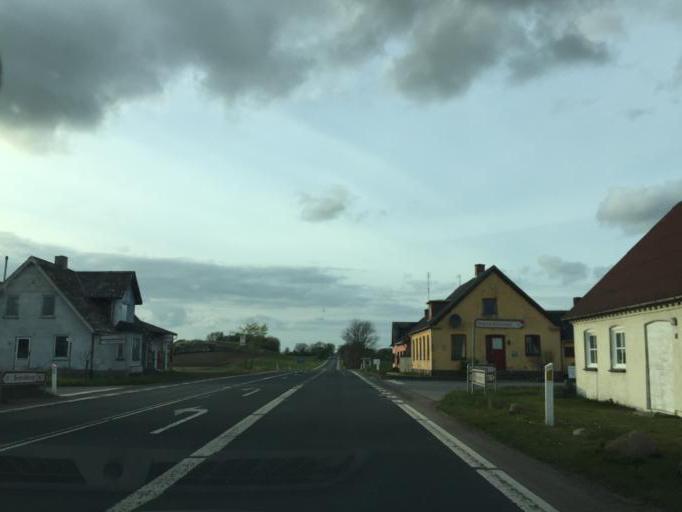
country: DK
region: South Denmark
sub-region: Svendborg Kommune
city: Svendborg
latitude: 55.1434
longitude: 10.5485
